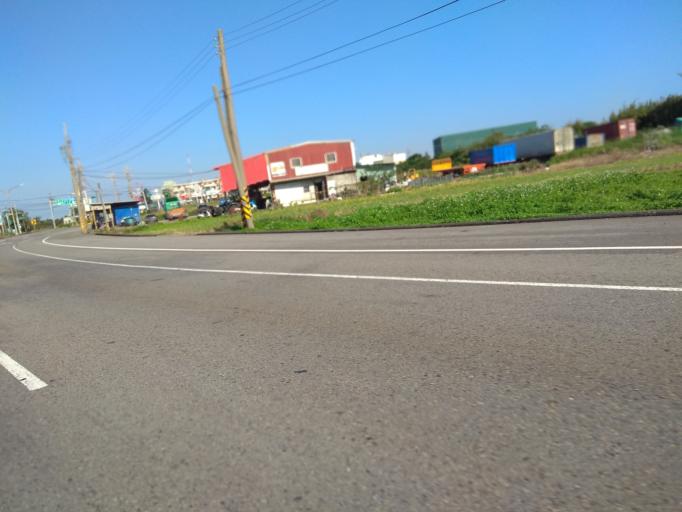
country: TW
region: Taiwan
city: Taoyuan City
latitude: 25.0325
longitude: 121.0937
